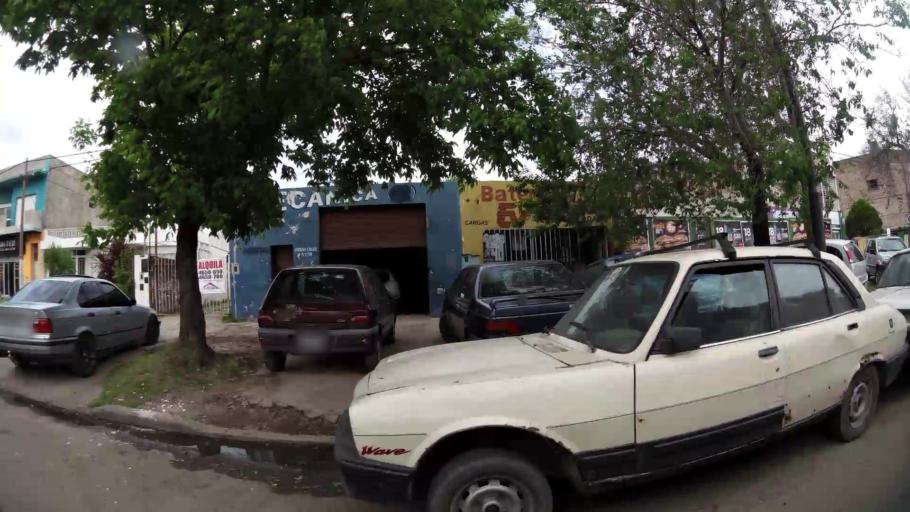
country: AR
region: Santa Fe
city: Gobernador Galvez
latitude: -33.0023
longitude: -60.6757
